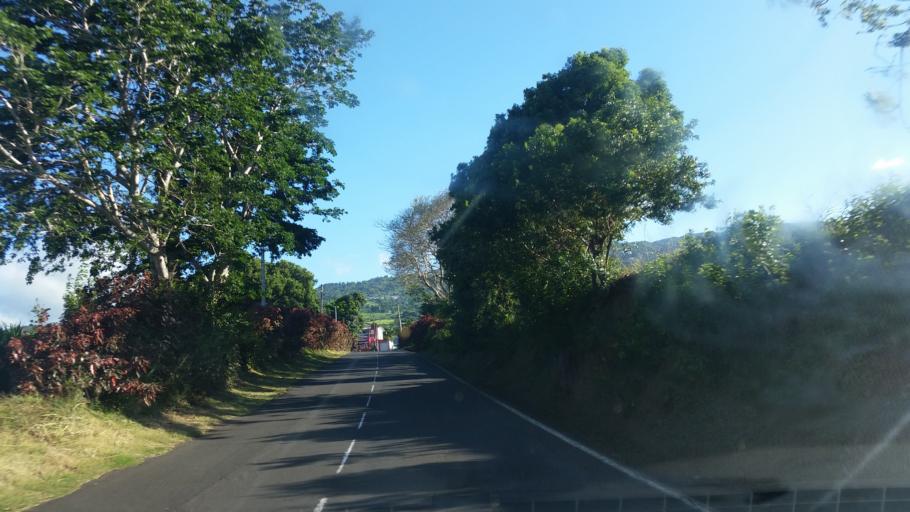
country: RE
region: Reunion
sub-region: Reunion
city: Sainte-Marie
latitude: -20.9287
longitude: 55.5306
